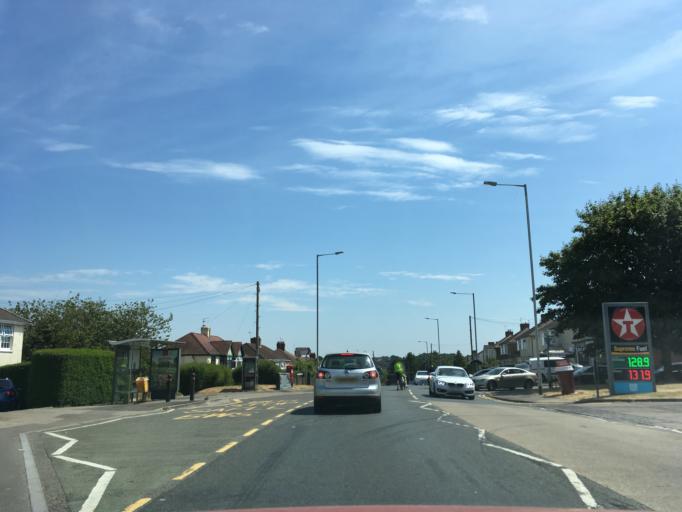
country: GB
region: Wales
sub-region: Newport
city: Newport
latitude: 51.5869
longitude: -3.0375
